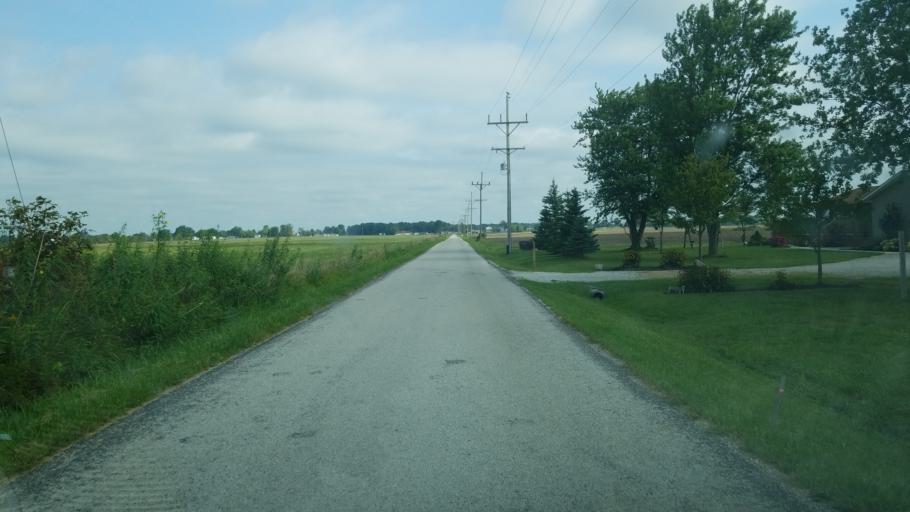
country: US
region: Ohio
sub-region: Marion County
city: Marion
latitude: 40.6029
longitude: -83.2031
